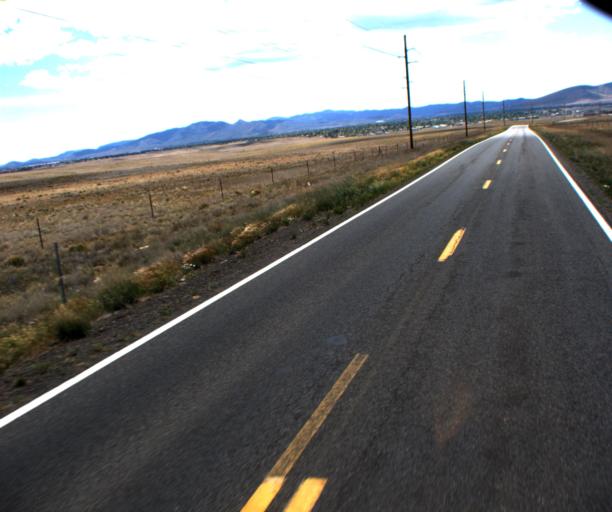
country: US
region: Arizona
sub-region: Yavapai County
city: Prescott Valley
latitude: 34.6474
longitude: -112.2945
